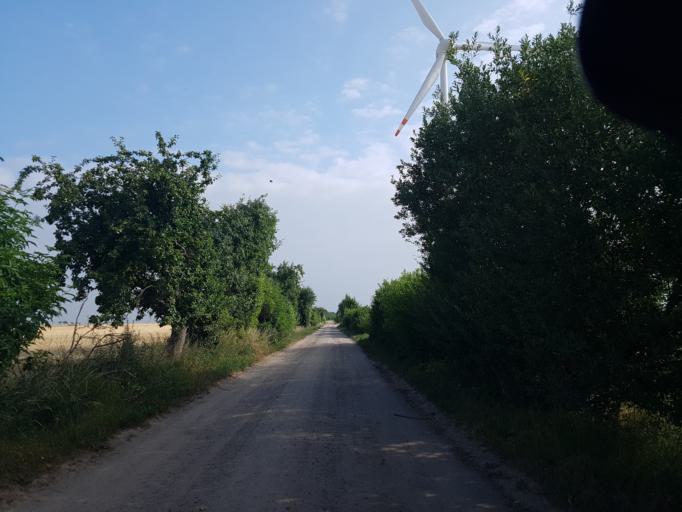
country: DE
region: Saxony-Anhalt
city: Kropstadt
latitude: 52.0010
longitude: 12.8189
